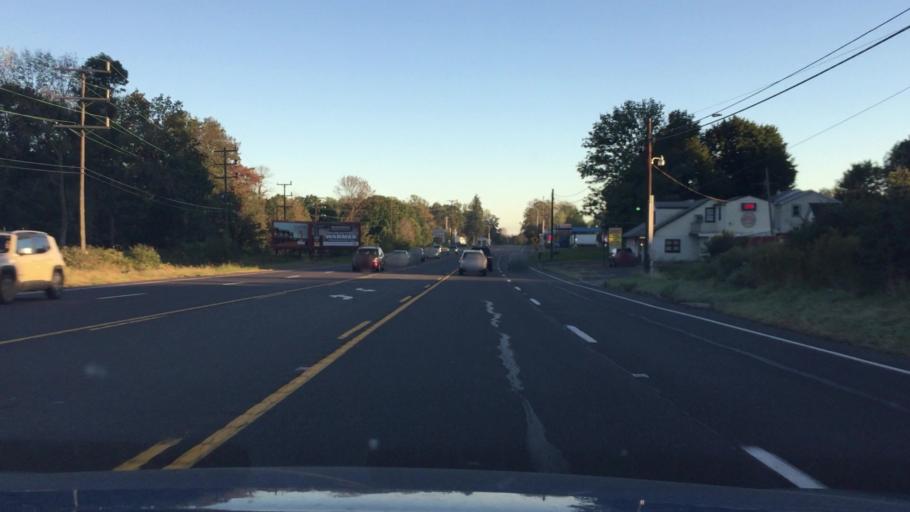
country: US
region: Pennsylvania
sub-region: Lehigh County
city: Coopersburg
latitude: 40.4948
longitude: -75.3817
